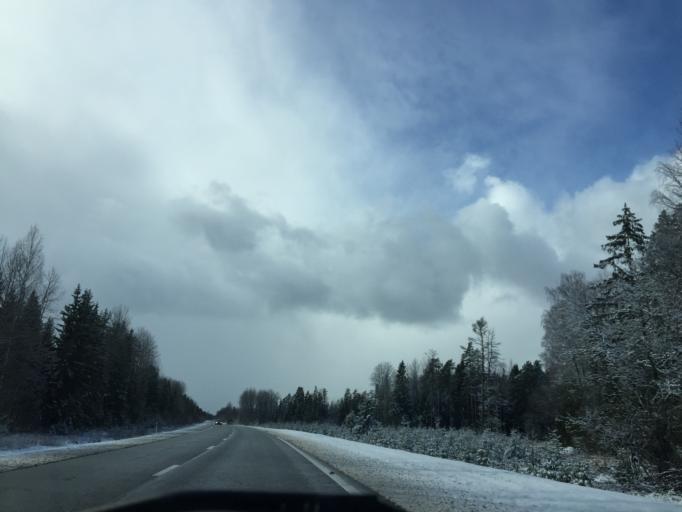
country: LV
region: Ventspils Rajons
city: Piltene
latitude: 57.3885
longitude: 21.7897
